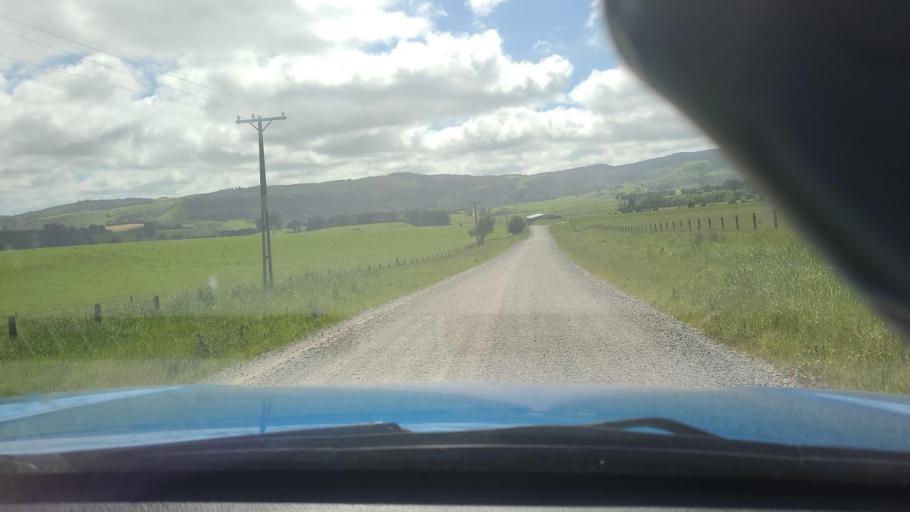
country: NZ
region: Southland
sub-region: Gore District
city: Gore
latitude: -46.3350
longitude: 168.9219
